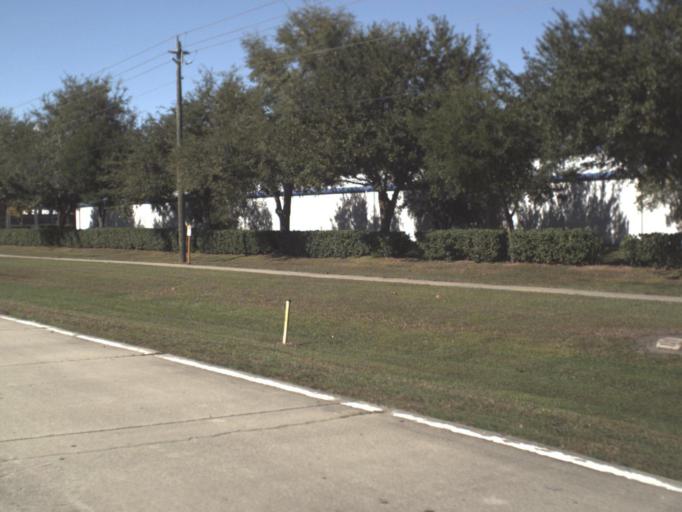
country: US
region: Florida
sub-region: Flagler County
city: Palm Coast
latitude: 29.5532
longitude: -81.2461
